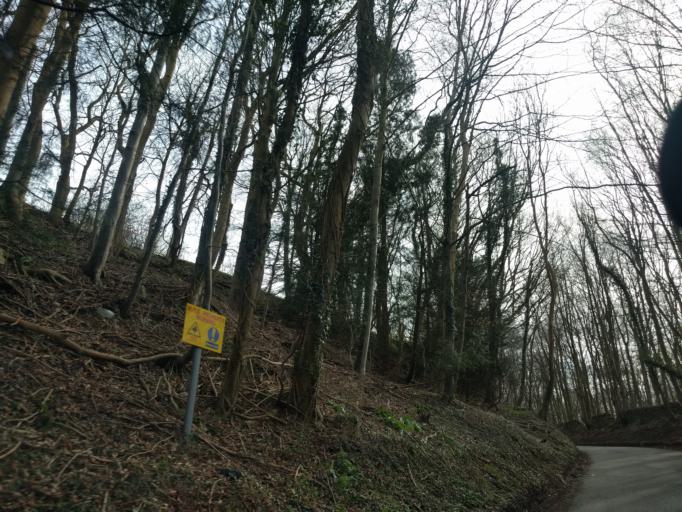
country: GB
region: England
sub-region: Wiltshire
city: Colerne
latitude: 51.4549
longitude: -2.2878
